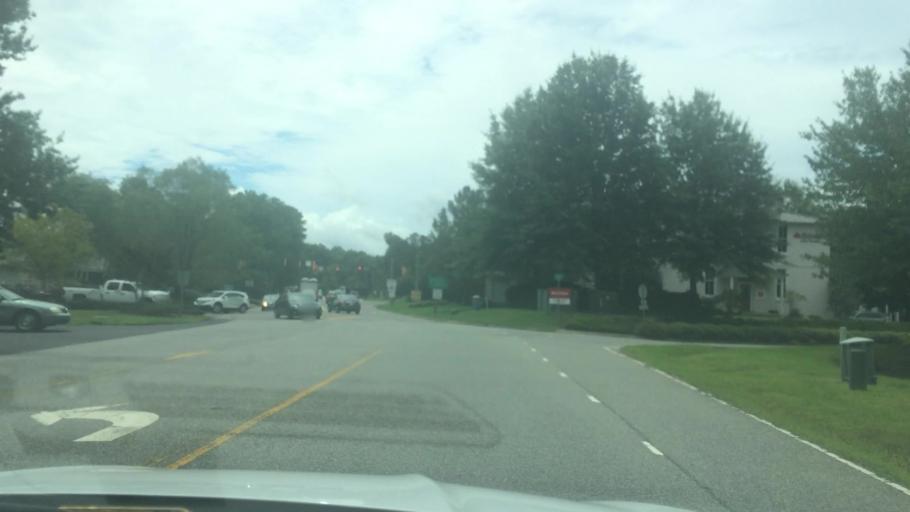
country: US
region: Virginia
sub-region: James City County
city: Williamsburg
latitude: 37.2534
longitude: -76.7658
